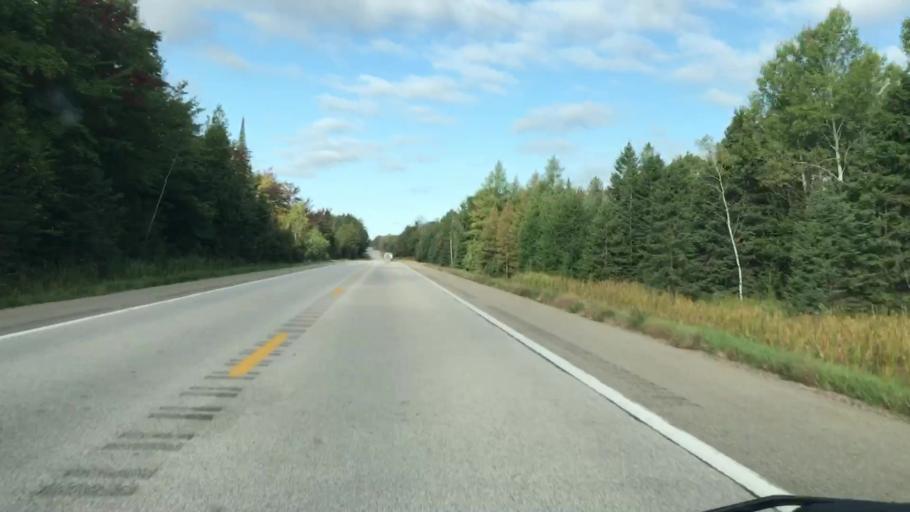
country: US
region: Michigan
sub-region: Luce County
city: Newberry
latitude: 46.3320
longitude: -85.0874
